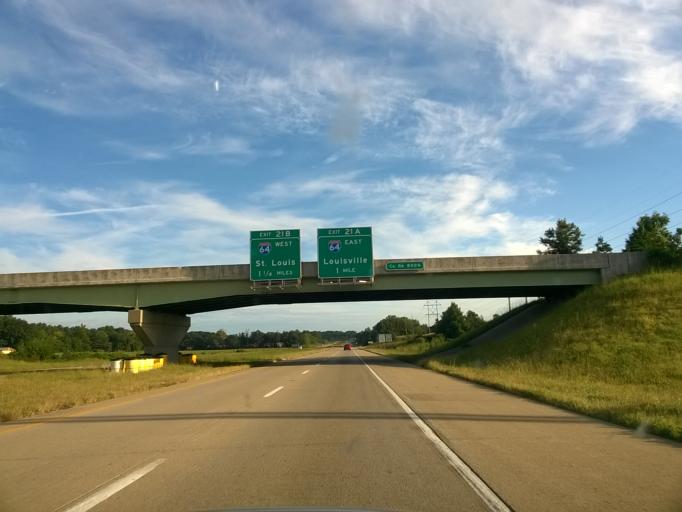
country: US
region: Indiana
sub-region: Gibson County
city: Haubstadt
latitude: 38.1515
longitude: -87.4725
